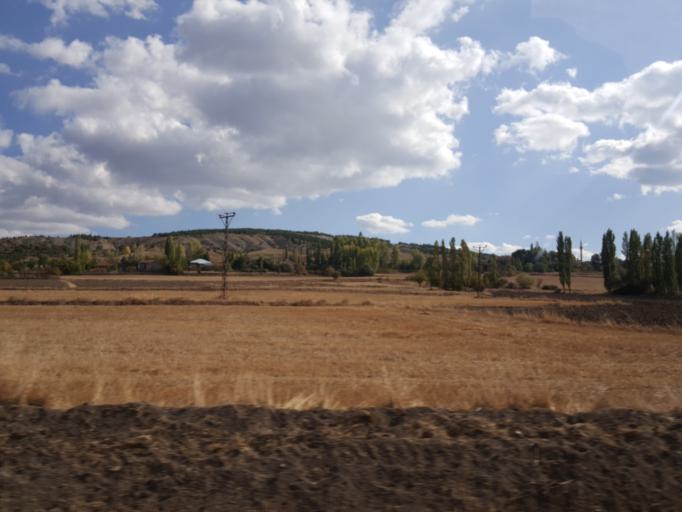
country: TR
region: Tokat
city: Sulusaray
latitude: 39.9886
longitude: 35.9919
